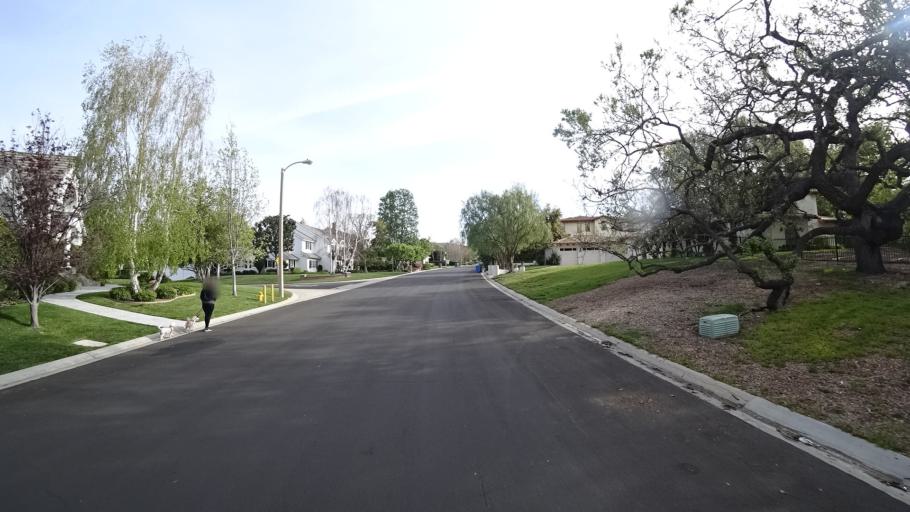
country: US
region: California
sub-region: Ventura County
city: Thousand Oaks
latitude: 34.1948
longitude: -118.8206
